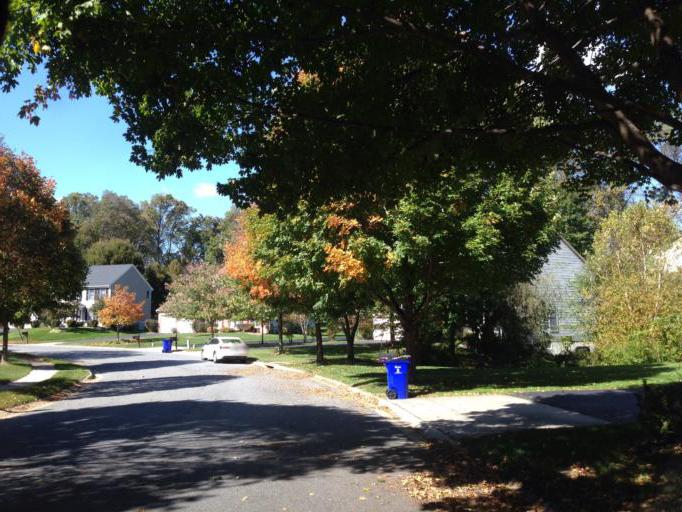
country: US
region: Maryland
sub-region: Howard County
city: North Laurel
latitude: 39.1361
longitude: -76.8946
